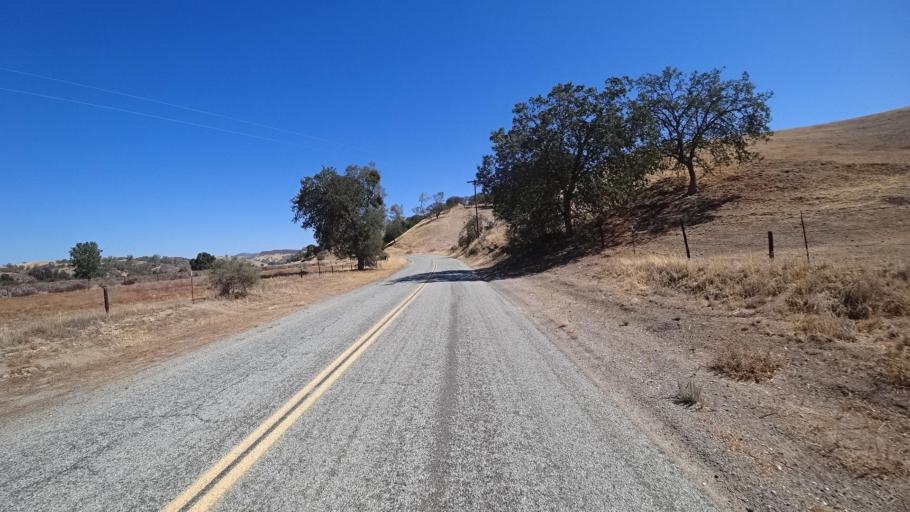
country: US
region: California
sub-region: San Luis Obispo County
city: San Miguel
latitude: 35.8418
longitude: -120.6178
